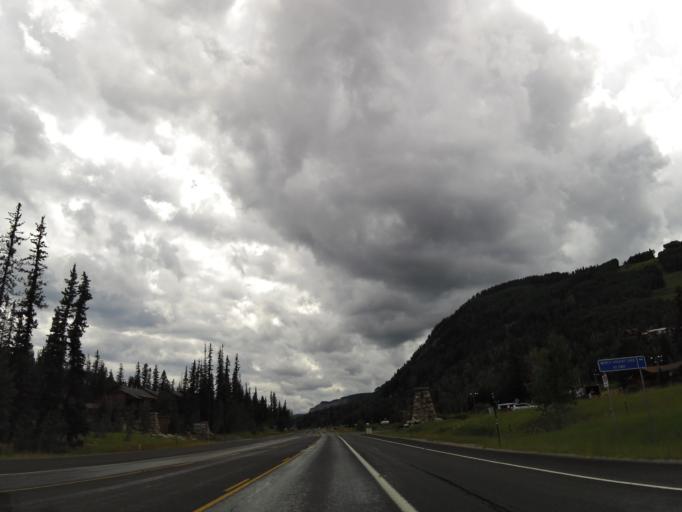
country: US
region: Colorado
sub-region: San Juan County
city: Silverton
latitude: 37.6292
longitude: -107.8095
